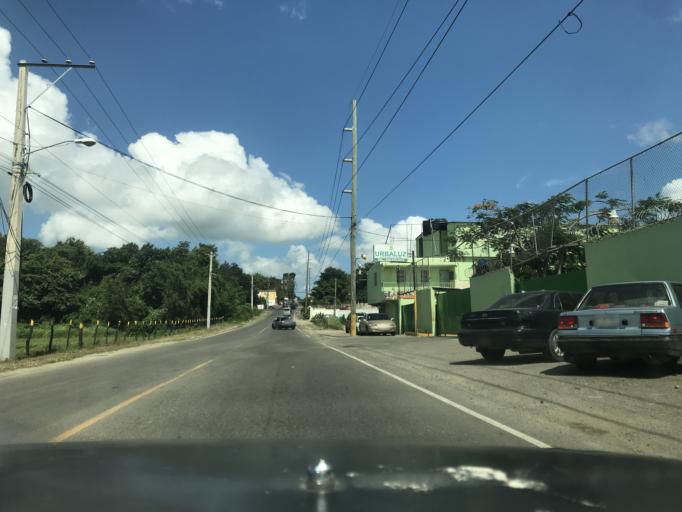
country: DO
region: Santiago
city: Santiago de los Caballeros
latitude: 19.4517
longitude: -70.7538
